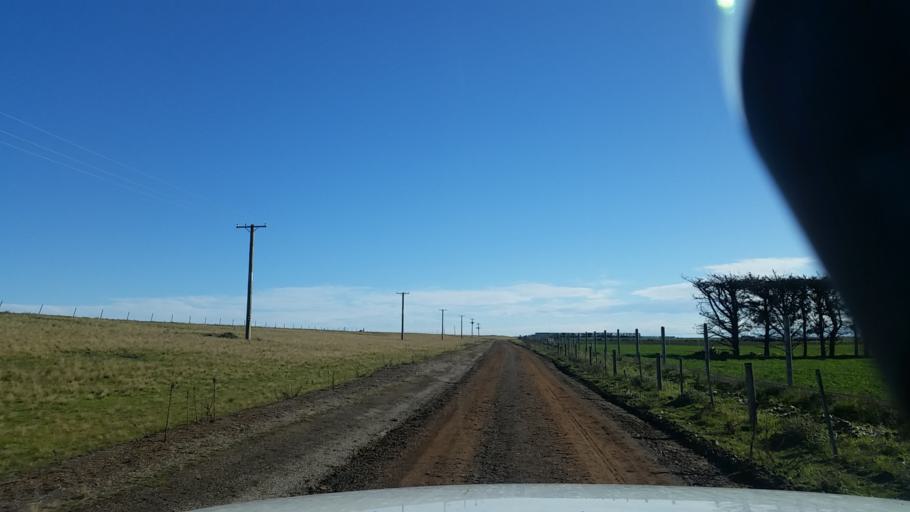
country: NZ
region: Canterbury
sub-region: Selwyn District
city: Lincoln
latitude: -43.8121
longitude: 172.6573
